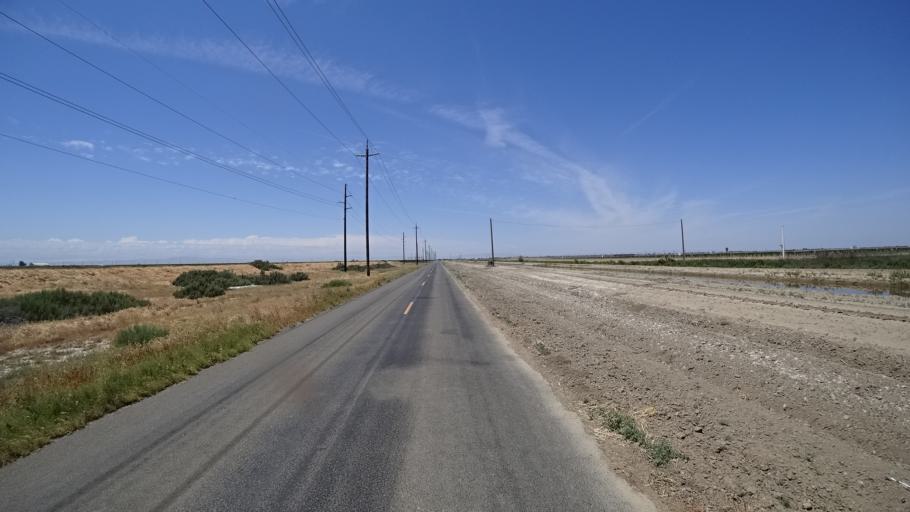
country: US
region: California
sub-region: Kings County
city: Stratford
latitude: 36.2406
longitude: -119.8211
